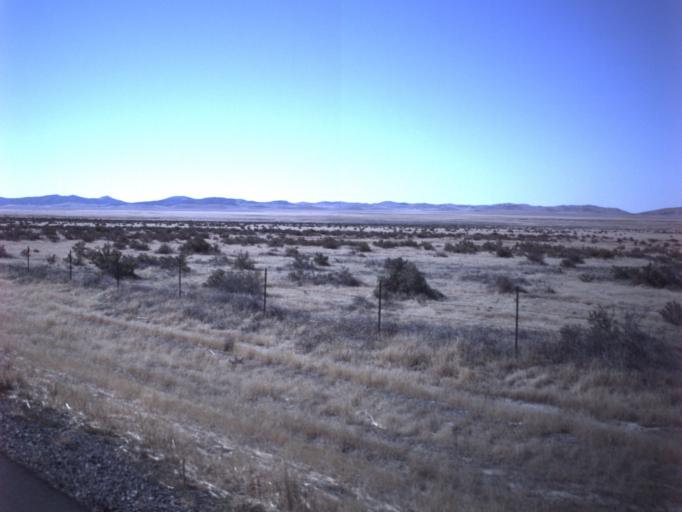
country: US
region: Utah
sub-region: Tooele County
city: Grantsville
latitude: 40.3645
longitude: -112.7461
